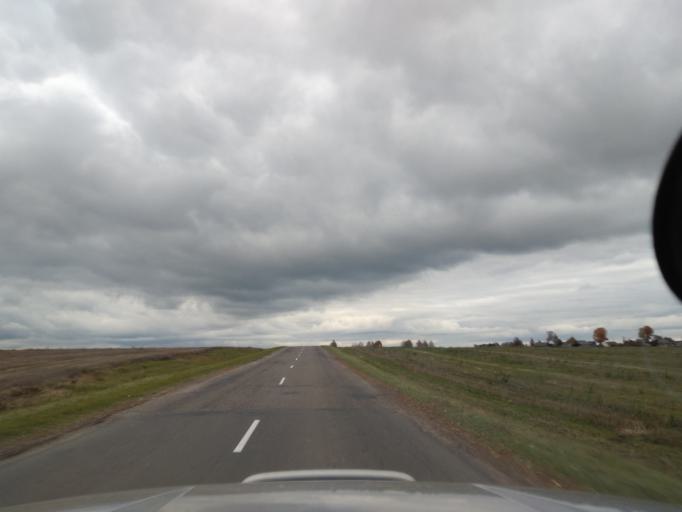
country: BY
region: Minsk
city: Slutsk
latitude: 53.2013
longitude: 27.3626
